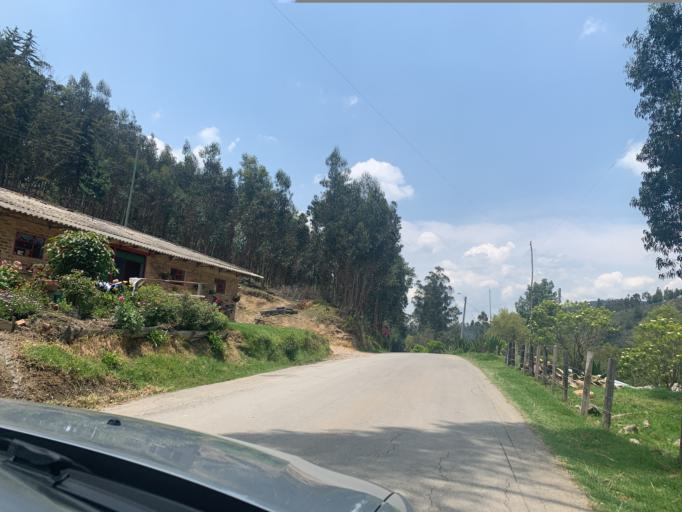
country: CO
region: Boyaca
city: Chiquinquira
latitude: 5.5479
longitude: -73.7518
